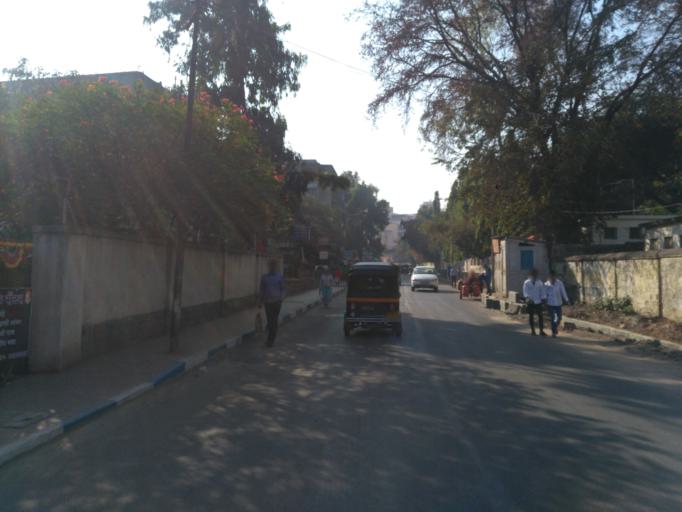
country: IN
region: Maharashtra
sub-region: Pune Division
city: Pune
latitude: 18.5120
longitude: 73.8717
